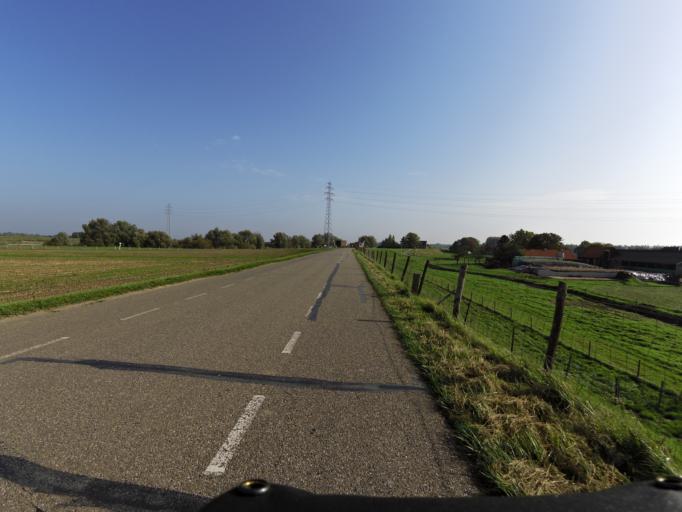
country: NL
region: Gelderland
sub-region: Gemeente Duiven
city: Duiven
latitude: 51.9046
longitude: 5.9946
